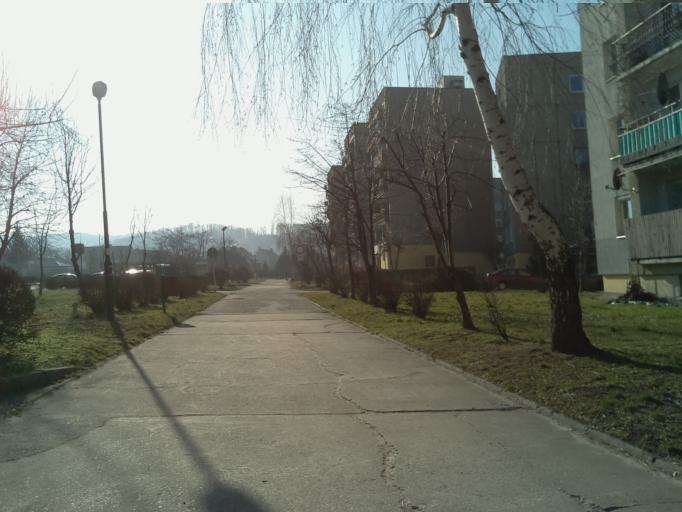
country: PL
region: Lower Silesian Voivodeship
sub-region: Powiat swidnicki
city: Swiebodzice
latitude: 50.8631
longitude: 16.3162
